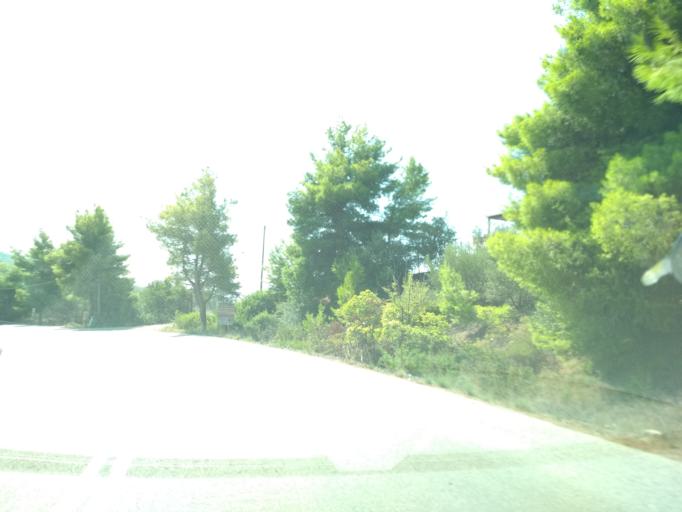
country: GR
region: Central Greece
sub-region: Nomos Evvoias
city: Roviai
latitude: 38.8179
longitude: 23.2298
